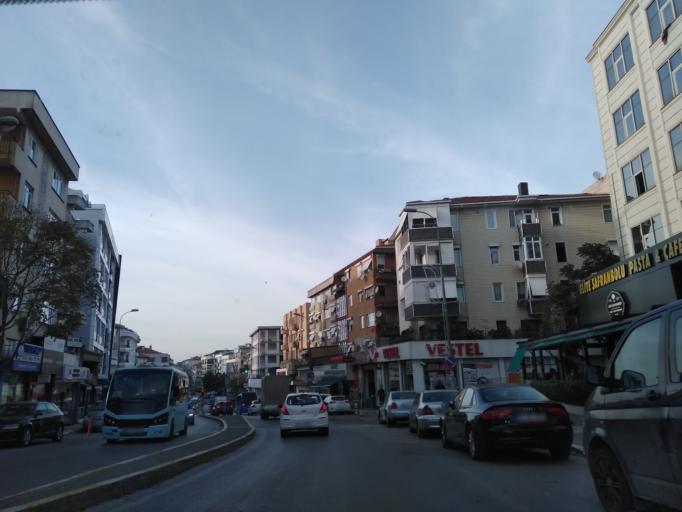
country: TR
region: Istanbul
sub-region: Atasehir
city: Atasehir
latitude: 40.9488
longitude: 29.1062
